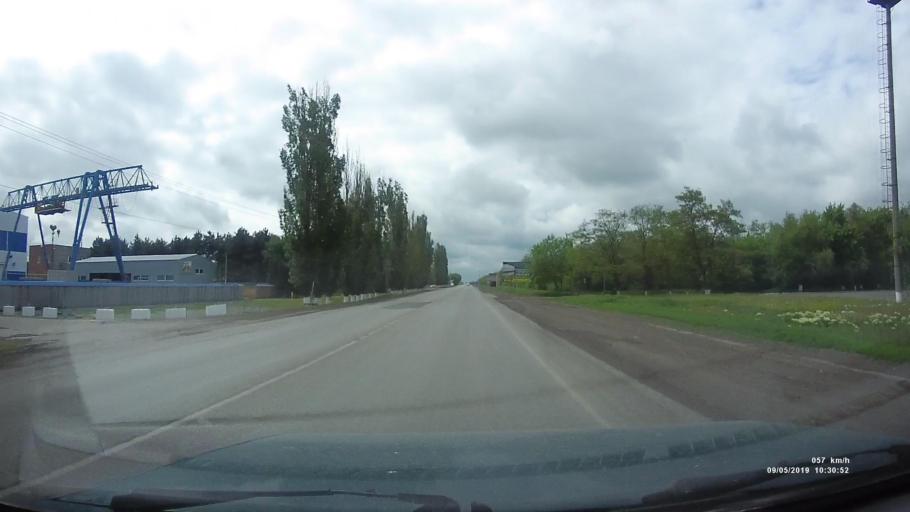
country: RU
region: Rostov
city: Azov
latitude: 47.0868
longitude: 39.4287
